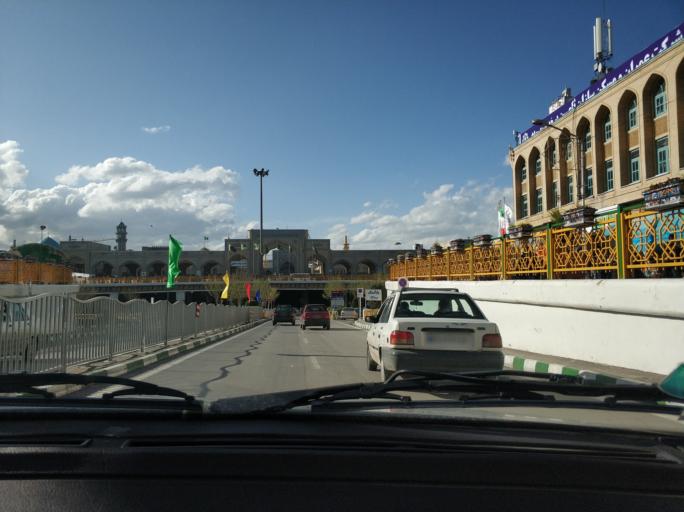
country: IR
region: Razavi Khorasan
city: Mashhad
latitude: 36.2857
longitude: 59.6191
